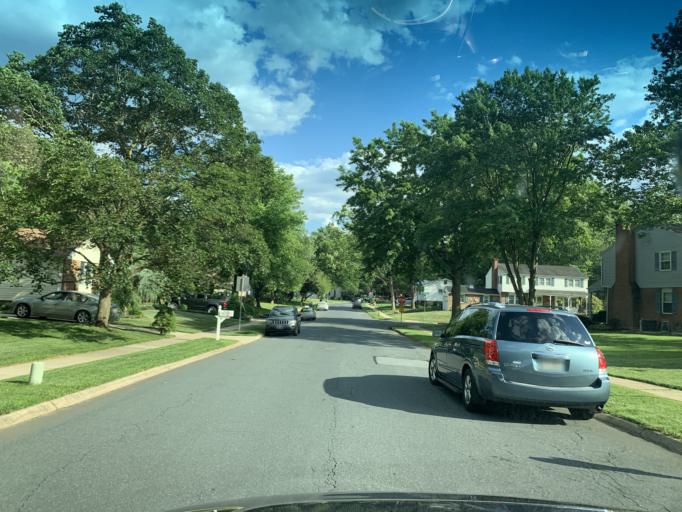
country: US
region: Maryland
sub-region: Harford County
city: Bel Air North
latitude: 39.5531
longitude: -76.3705
